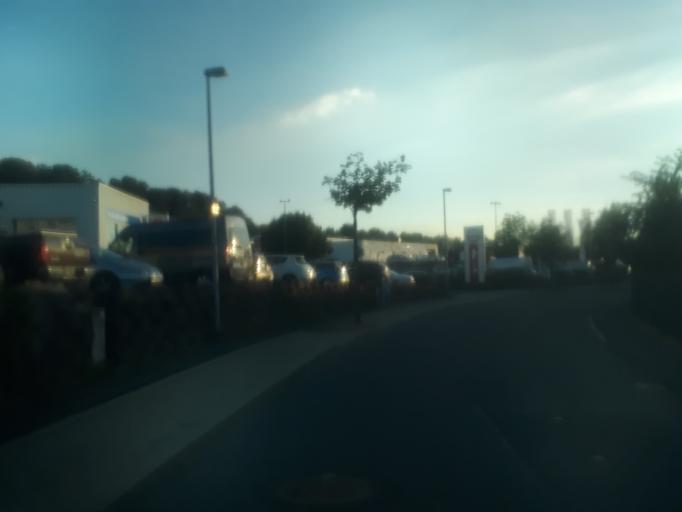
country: DE
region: Saxony
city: Radeberg
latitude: 51.0654
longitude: 13.8979
